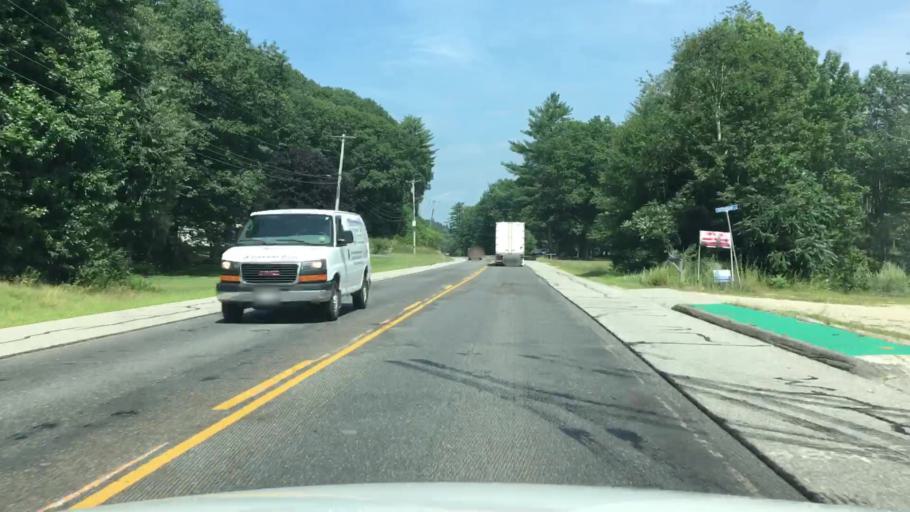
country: US
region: Maine
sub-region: Androscoggin County
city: Turner
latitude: 44.3063
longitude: -70.2665
